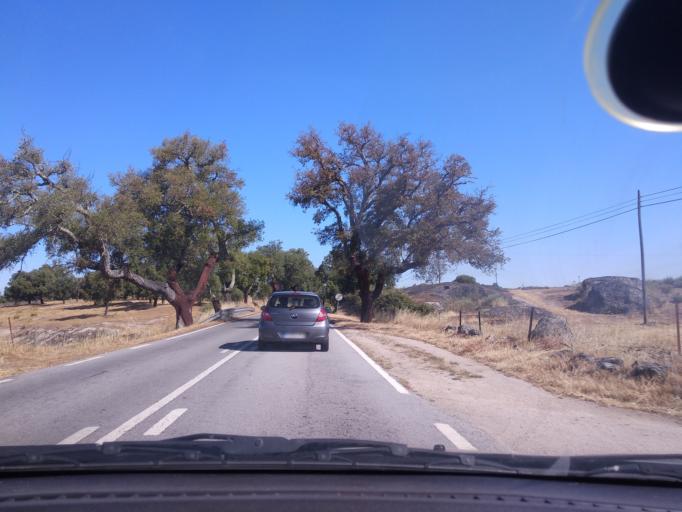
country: PT
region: Portalegre
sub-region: Nisa
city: Nisa
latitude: 39.4943
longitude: -7.6409
